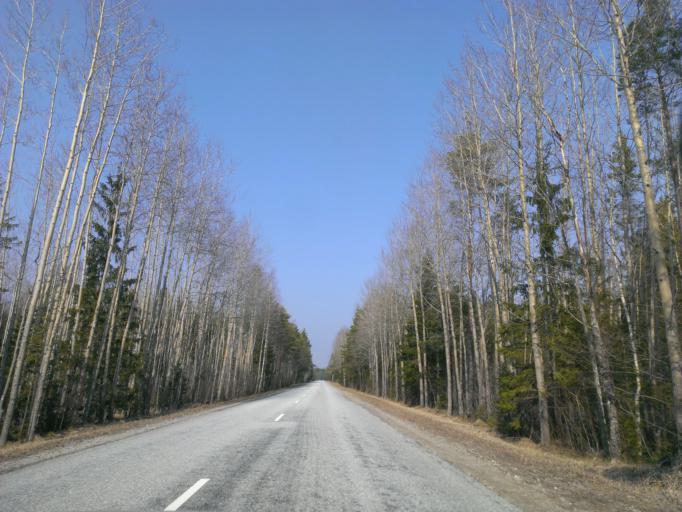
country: EE
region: Saare
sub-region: Kuressaare linn
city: Kuressaare
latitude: 58.3511
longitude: 22.6768
